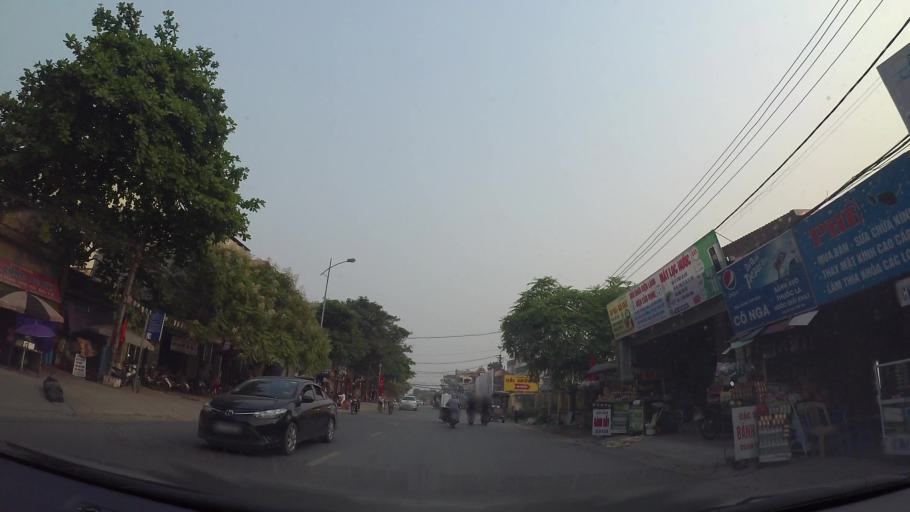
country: VN
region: Ha Noi
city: Thuong Tin
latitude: 20.8705
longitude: 105.8648
